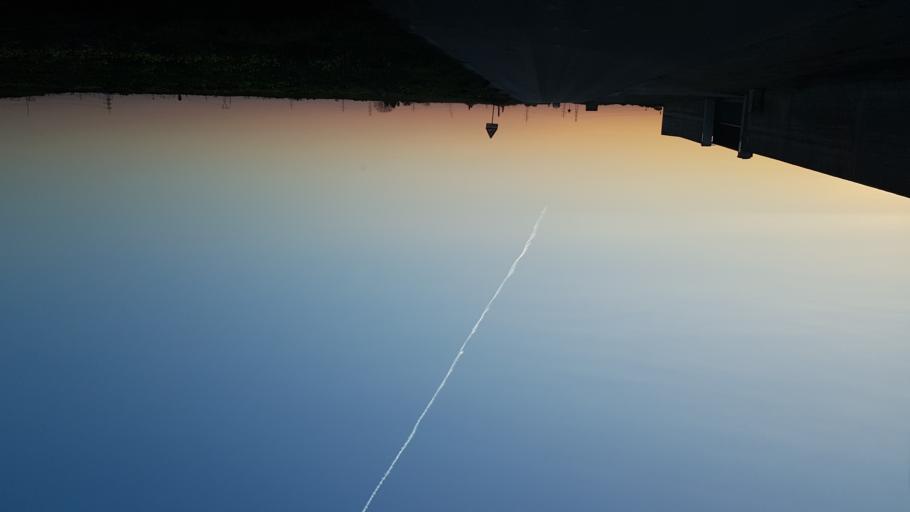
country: IT
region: Apulia
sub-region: Provincia di Brindisi
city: La Rosa
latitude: 40.5903
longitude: 17.9226
